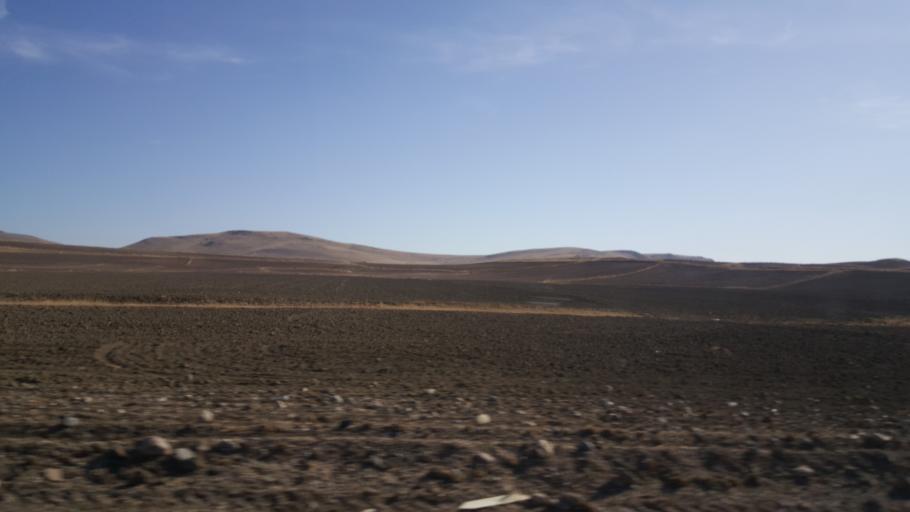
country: TR
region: Ankara
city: Yenice
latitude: 39.3559
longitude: 32.7933
